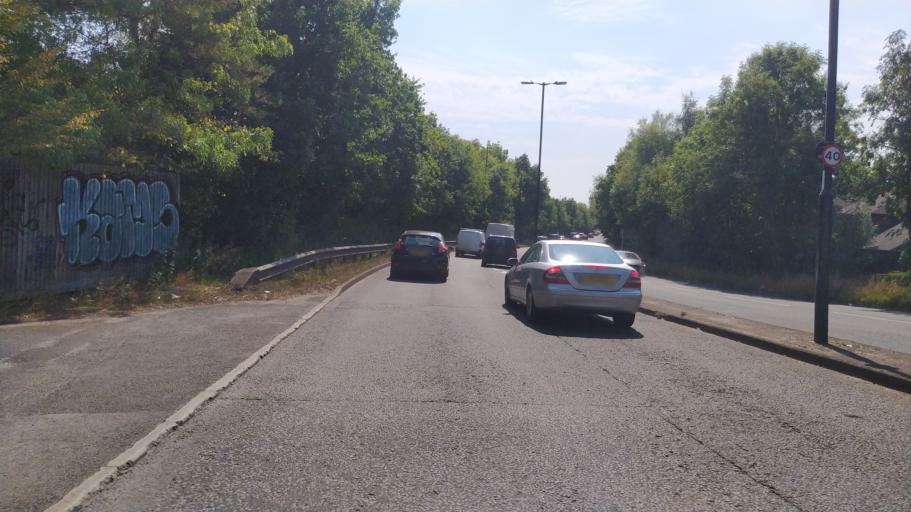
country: GB
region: England
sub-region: Southampton
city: Southampton
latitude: 50.9245
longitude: -1.3872
